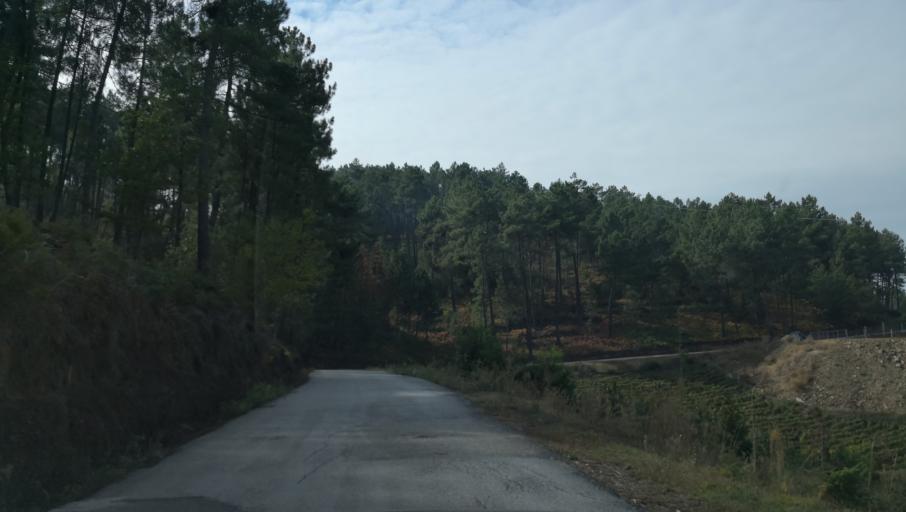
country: PT
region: Vila Real
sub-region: Sabrosa
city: Vilela
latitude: 41.2286
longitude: -7.6851
